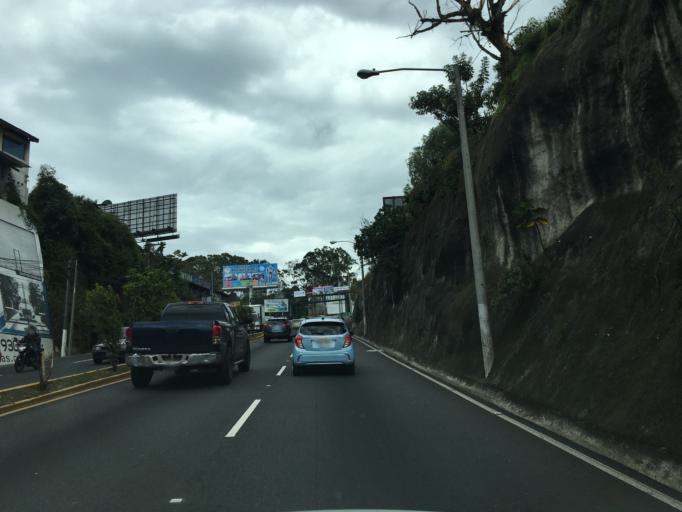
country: GT
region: Guatemala
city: Mixco
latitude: 14.5953
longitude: -90.5692
